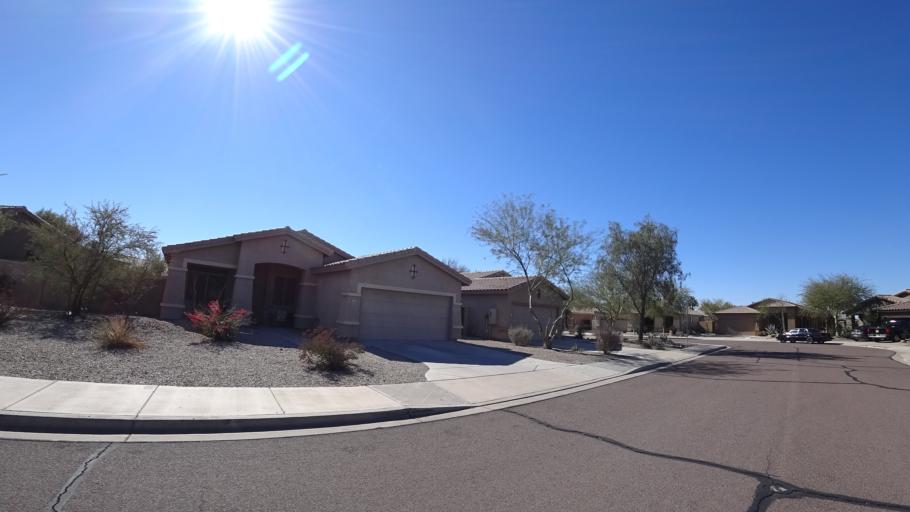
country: US
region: Arizona
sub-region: Maricopa County
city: Goodyear
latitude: 33.3535
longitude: -112.4271
